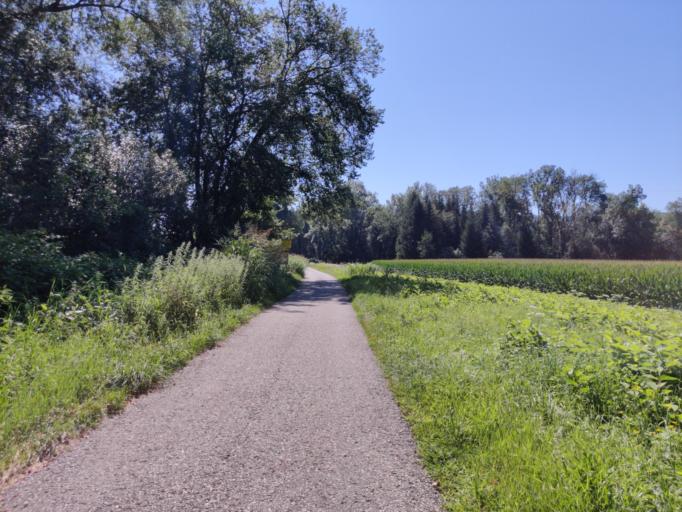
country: AT
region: Styria
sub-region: Politischer Bezirk Leibnitz
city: Wildon
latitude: 46.8972
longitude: 15.4978
